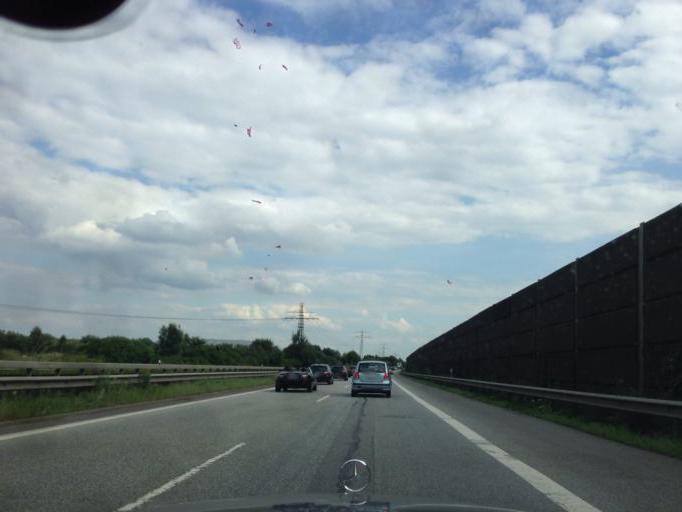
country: DE
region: Hamburg
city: Rothenburgsort
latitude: 53.5009
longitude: 10.0884
